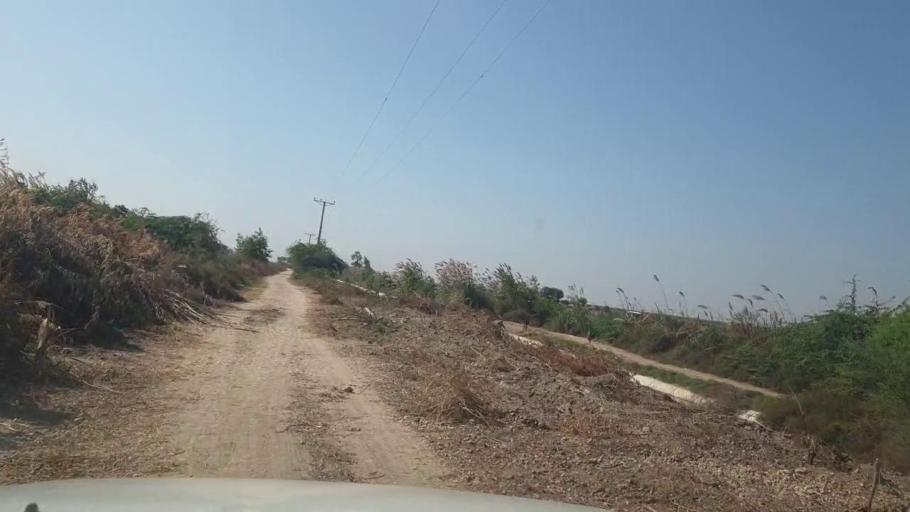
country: PK
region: Sindh
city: Chuhar Jamali
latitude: 24.4225
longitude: 67.8162
